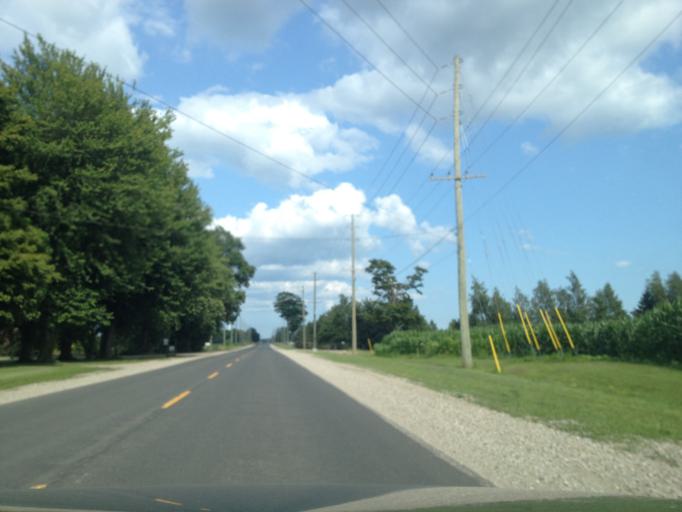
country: CA
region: Ontario
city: Aylmer
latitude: 42.6740
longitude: -80.8796
